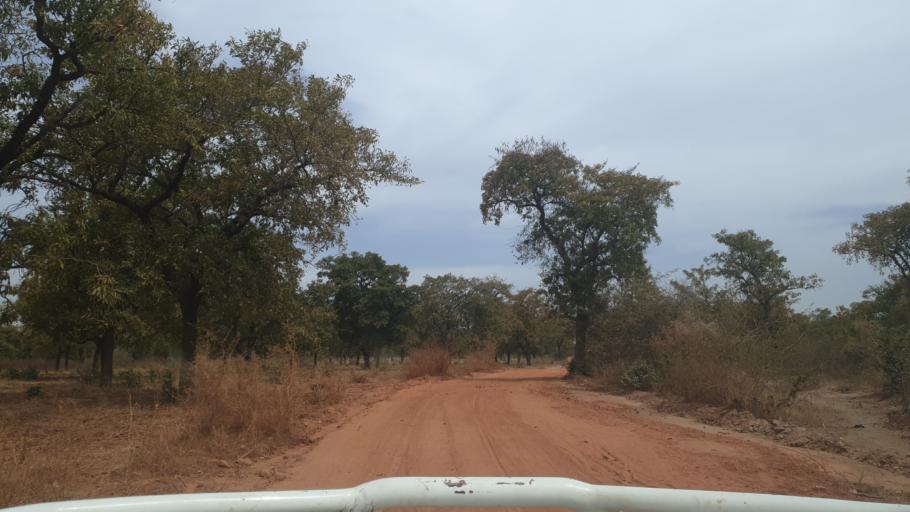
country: ML
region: Sikasso
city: Yorosso
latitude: 12.2266
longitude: -4.7510
